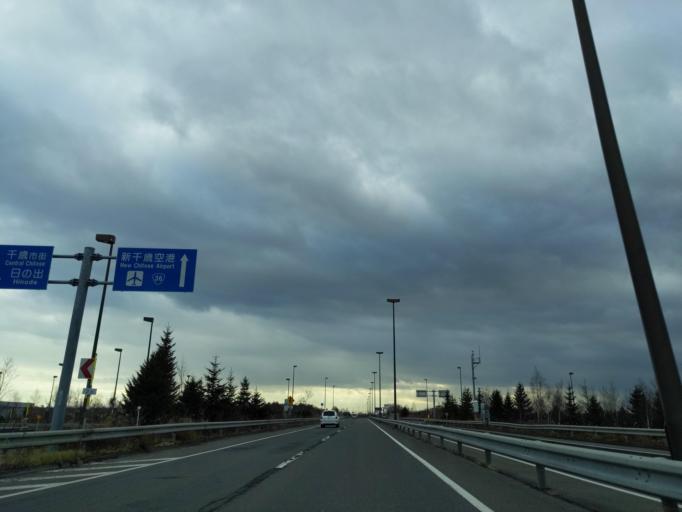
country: JP
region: Hokkaido
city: Chitose
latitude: 42.8203
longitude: 141.6841
